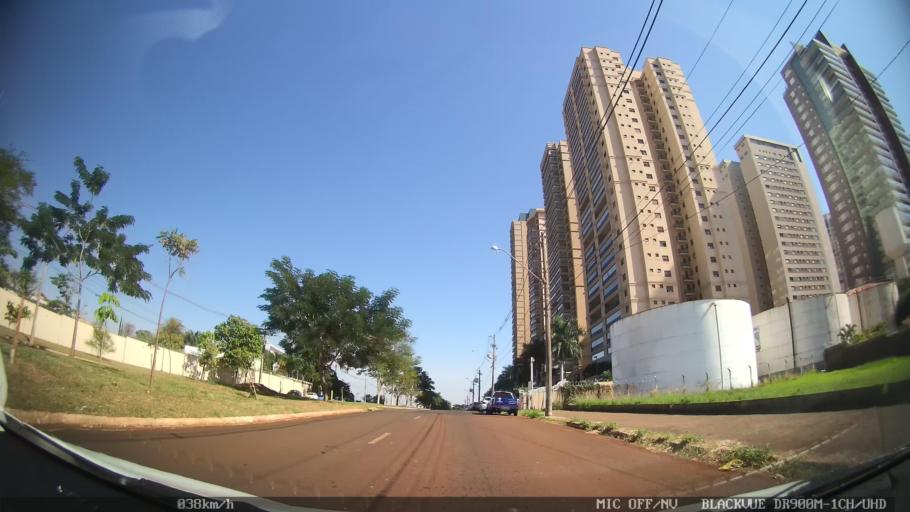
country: BR
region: Sao Paulo
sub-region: Ribeirao Preto
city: Ribeirao Preto
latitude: -21.2194
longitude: -47.8027
